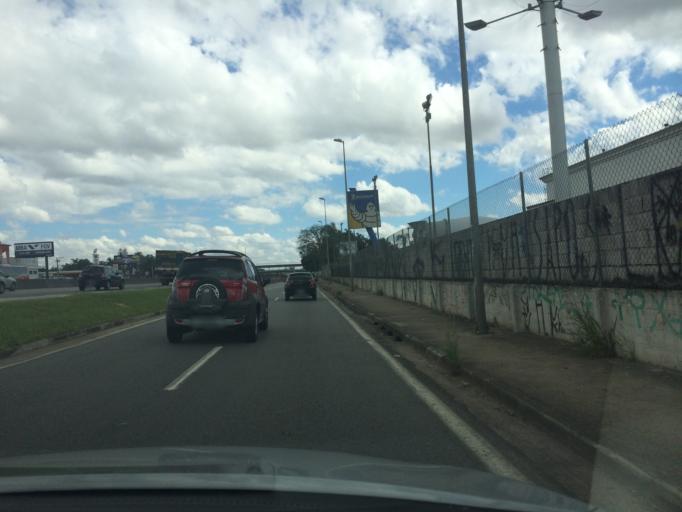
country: BR
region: Sao Paulo
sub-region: Guarulhos
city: Guarulhos
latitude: -23.4737
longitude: -46.5227
